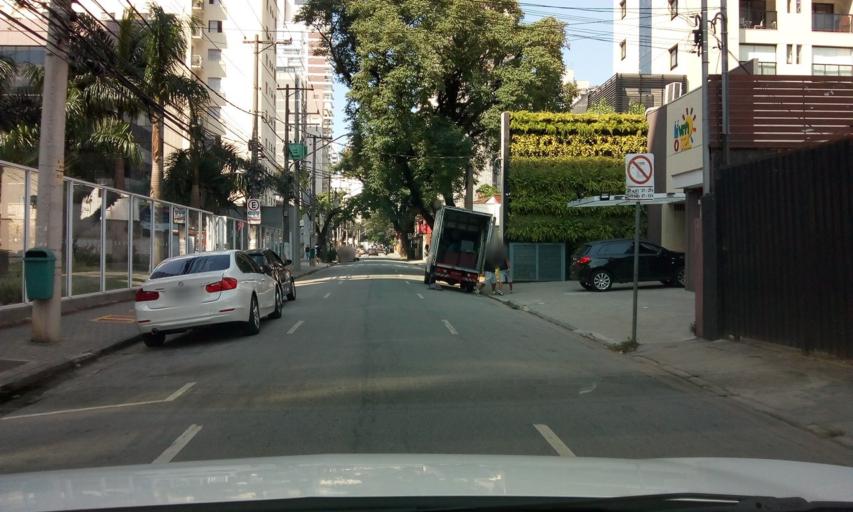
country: BR
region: Sao Paulo
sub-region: Sao Paulo
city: Sao Paulo
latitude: -23.5995
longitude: -46.6825
